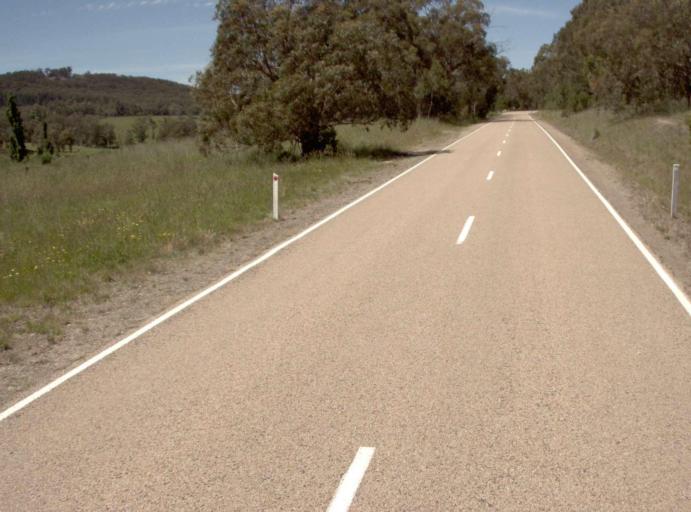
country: AU
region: Victoria
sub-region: East Gippsland
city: Lakes Entrance
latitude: -37.2076
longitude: 148.2693
